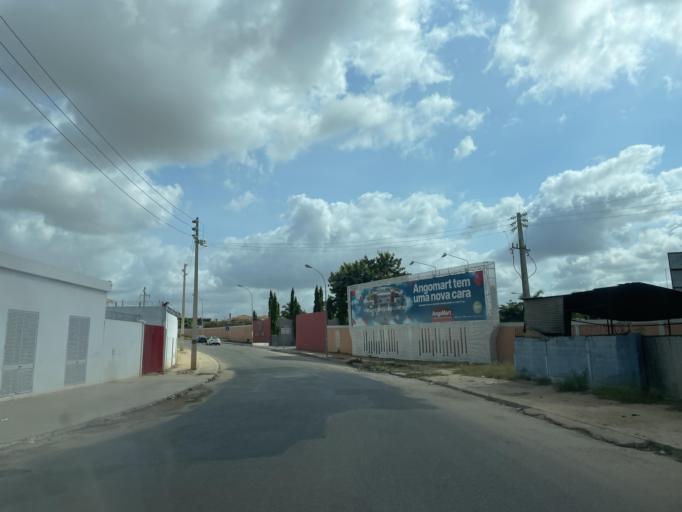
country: AO
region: Luanda
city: Luanda
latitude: -8.9198
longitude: 13.2045
